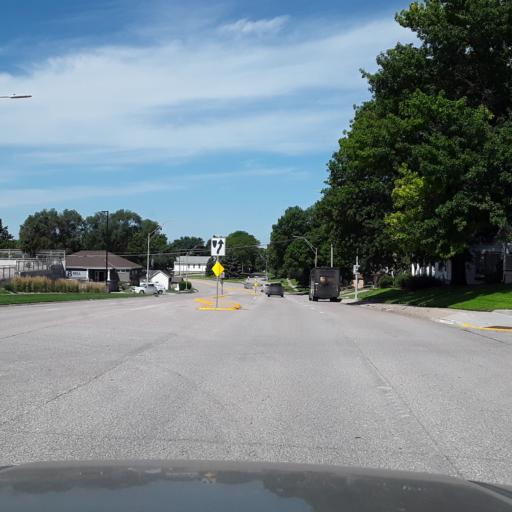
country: US
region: Nebraska
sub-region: Seward County
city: Seward
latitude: 40.9070
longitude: -97.1012
